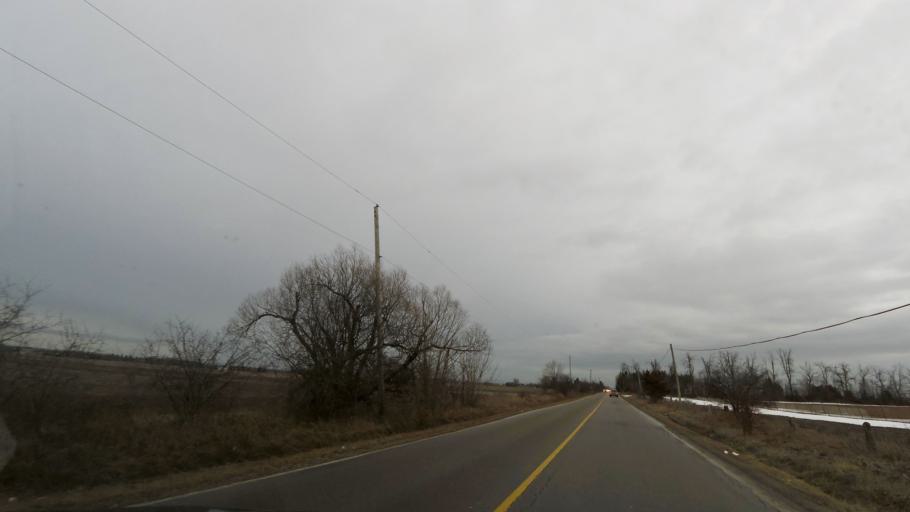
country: CA
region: Ontario
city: Brampton
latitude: 43.8303
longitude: -79.6944
